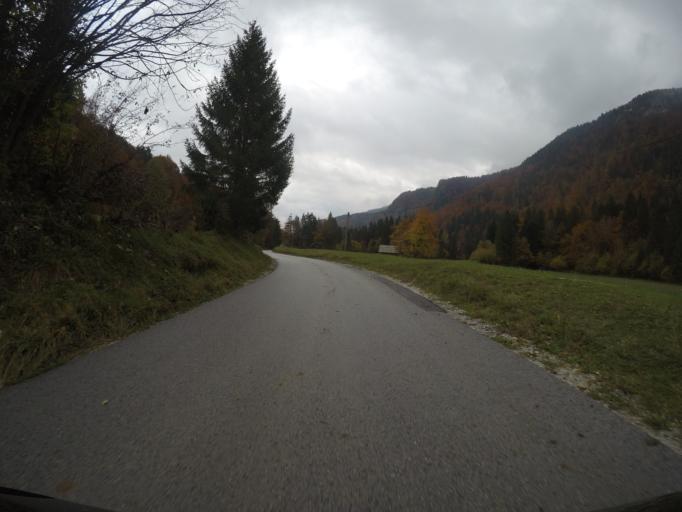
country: SI
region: Jesenice
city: Hrusica
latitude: 46.3935
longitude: 14.0180
